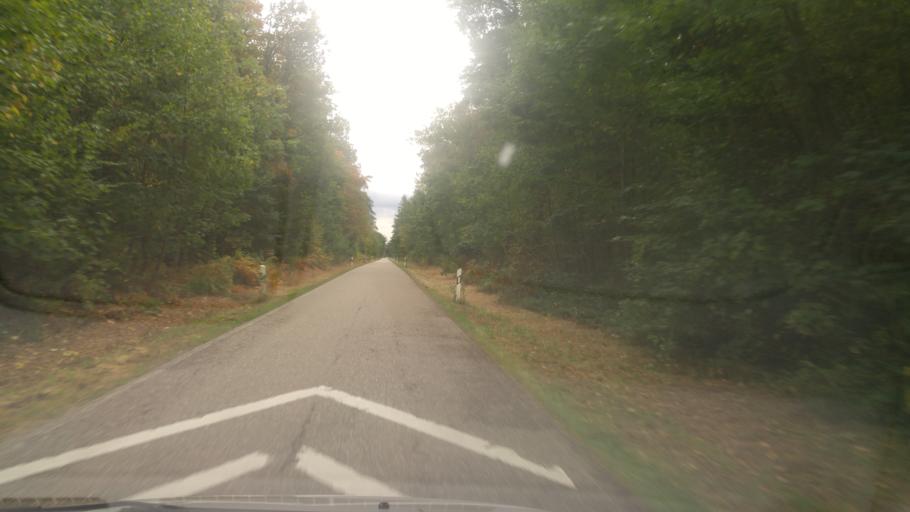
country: DE
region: Rheinland-Pfalz
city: Steinfeld
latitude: 48.9982
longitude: 8.0763
